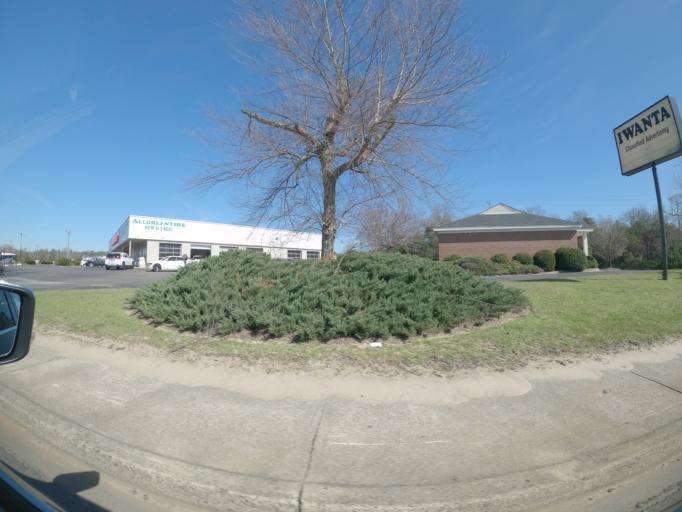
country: US
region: South Carolina
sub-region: Aiken County
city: North Augusta
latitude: 33.4895
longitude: -81.9509
